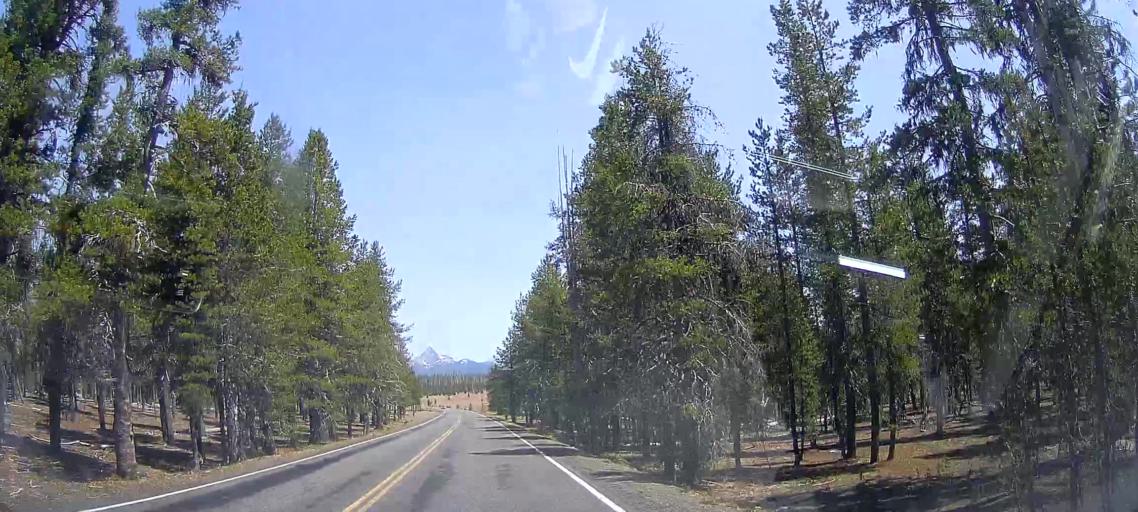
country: US
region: Oregon
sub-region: Lane County
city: Oakridge
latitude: 43.0259
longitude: -122.1200
